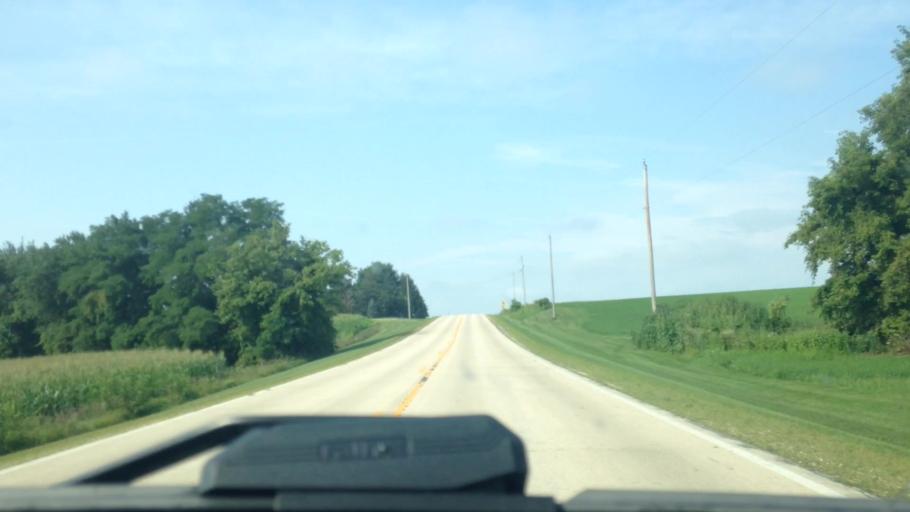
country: US
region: Wisconsin
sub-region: Dodge County
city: Mayville
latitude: 43.5235
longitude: -88.5104
